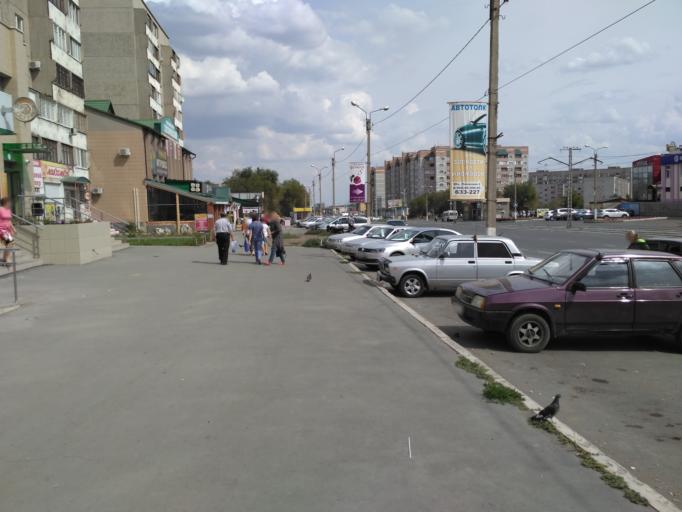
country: RU
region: Orenburg
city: Novotroitsk
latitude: 51.1917
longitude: 58.2836
